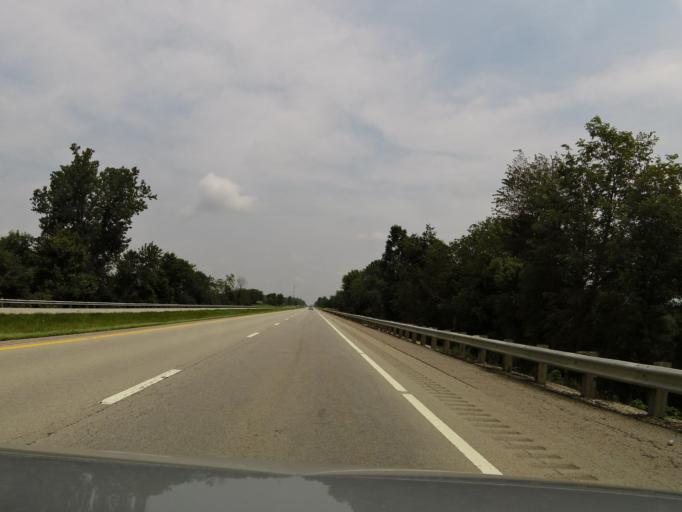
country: US
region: Kentucky
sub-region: Hardin County
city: Elizabethtown
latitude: 37.6036
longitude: -85.9800
